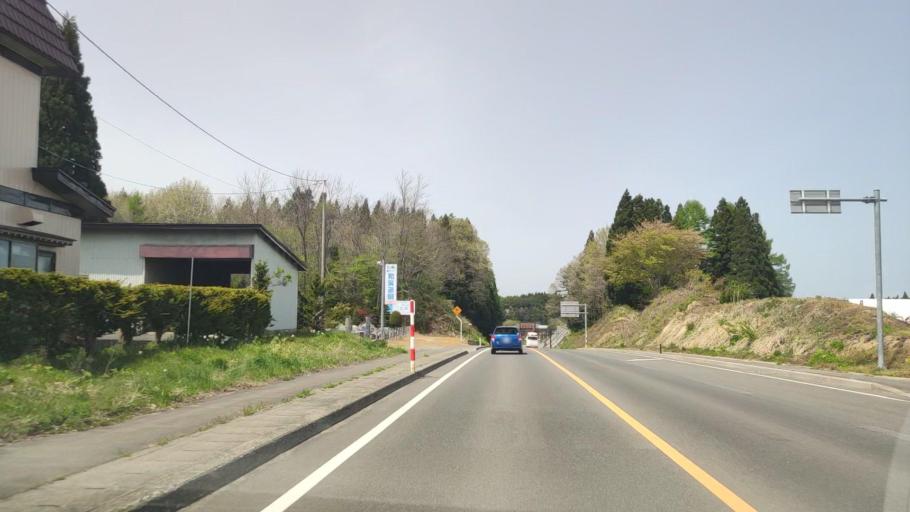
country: JP
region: Aomori
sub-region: Misawa Shi
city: Inuotose
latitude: 40.6603
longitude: 141.1905
